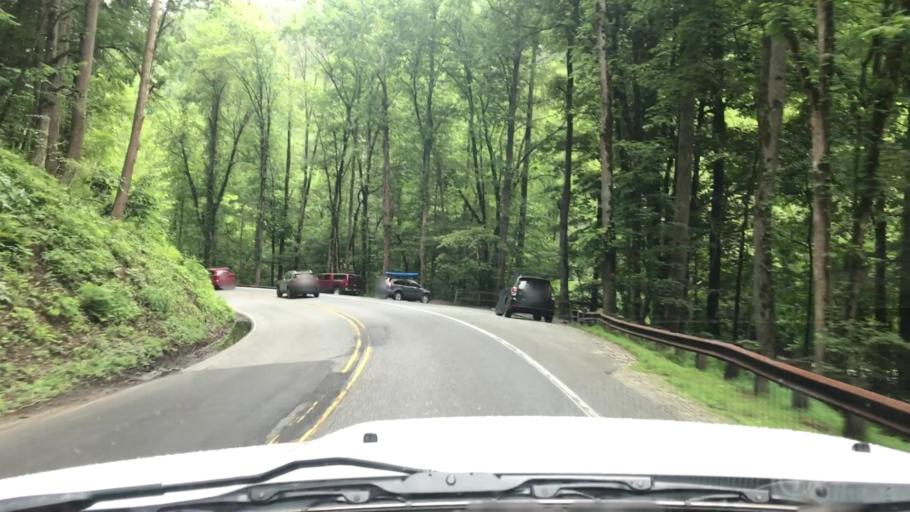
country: US
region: North Carolina
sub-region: Graham County
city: Robbinsville
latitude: 35.3331
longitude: -83.6272
